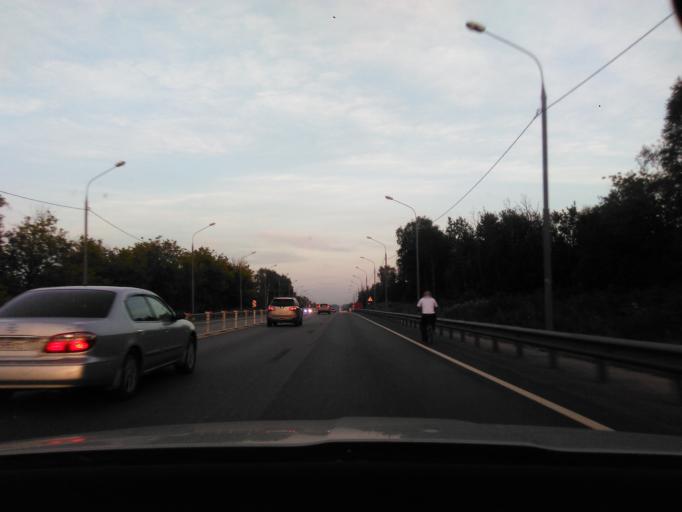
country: RU
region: Moskovskaya
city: Klin
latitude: 56.3130
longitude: 36.7744
